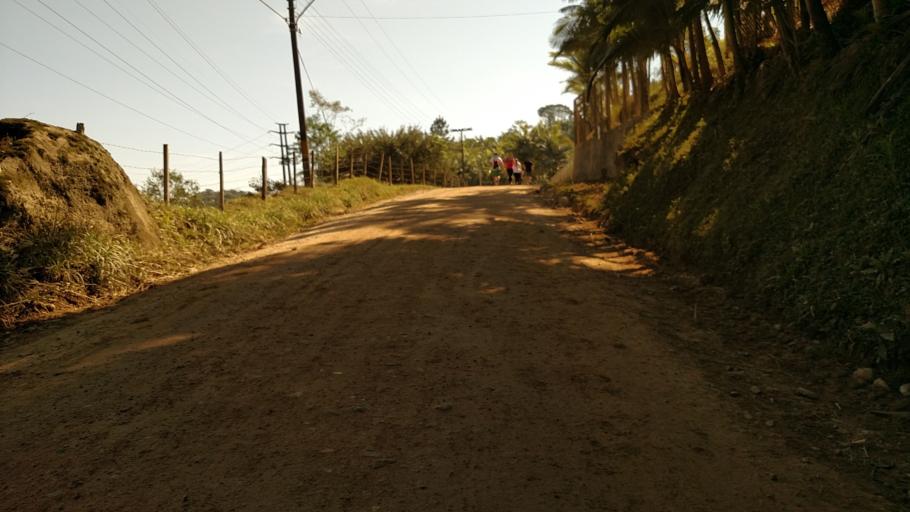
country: BR
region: Santa Catarina
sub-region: Pomerode
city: Pomerode
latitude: -26.7313
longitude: -49.0944
